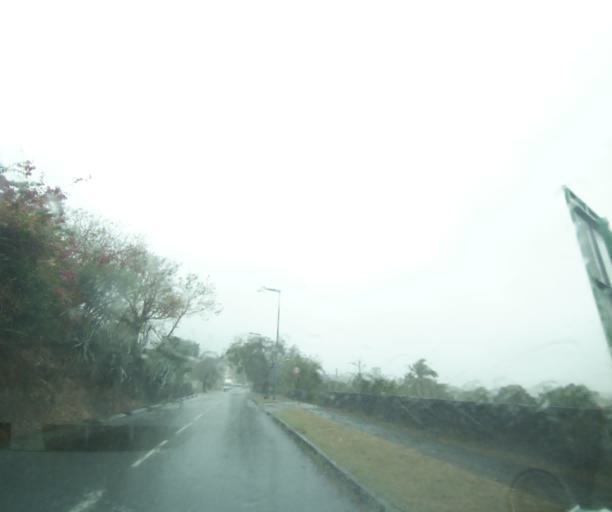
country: RE
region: Reunion
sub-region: Reunion
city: Saint-Paul
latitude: -21.0281
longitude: 55.2652
